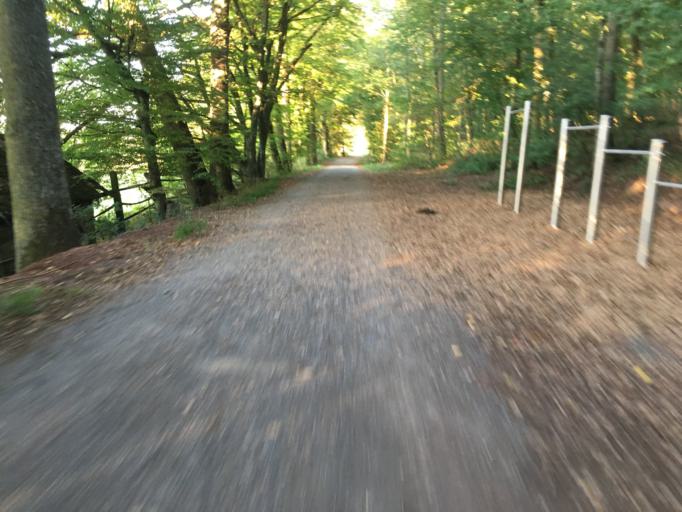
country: DE
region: Baden-Wuerttemberg
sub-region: Regierungsbezirk Stuttgart
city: Boeblingen
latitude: 48.6699
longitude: 8.9879
